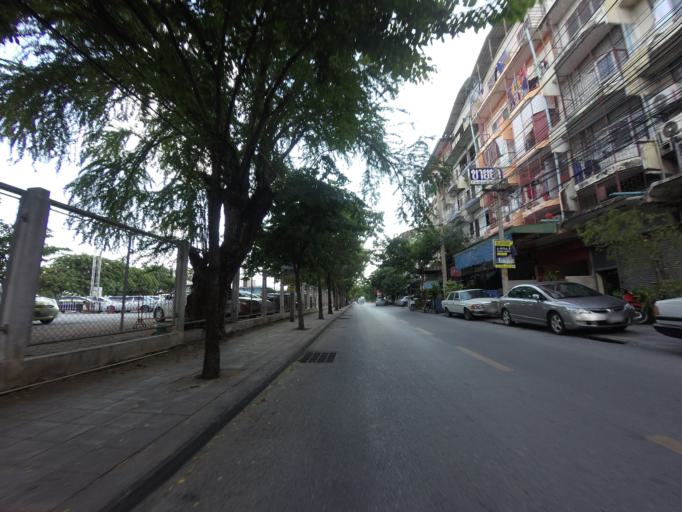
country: TH
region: Bangkok
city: Bang Sue
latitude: 13.8023
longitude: 100.5562
